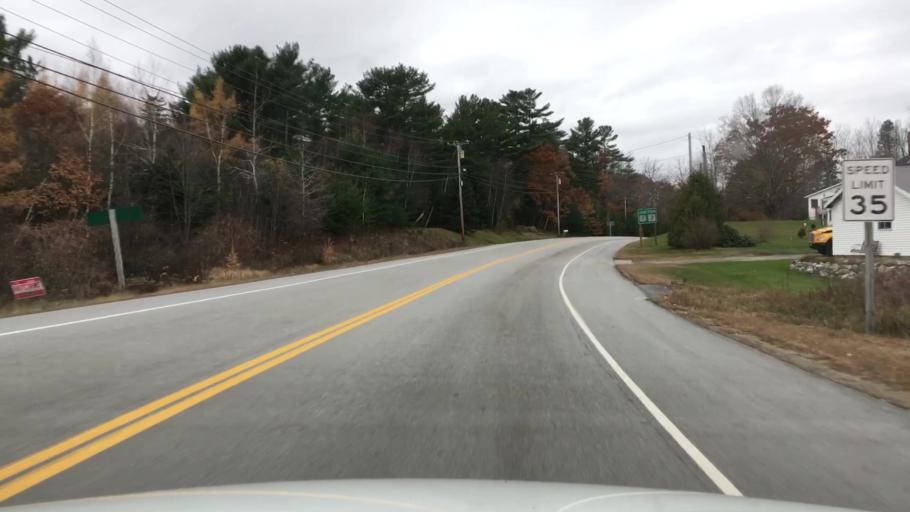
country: US
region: Maine
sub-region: Hancock County
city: Orland
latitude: 44.5588
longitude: -68.7060
